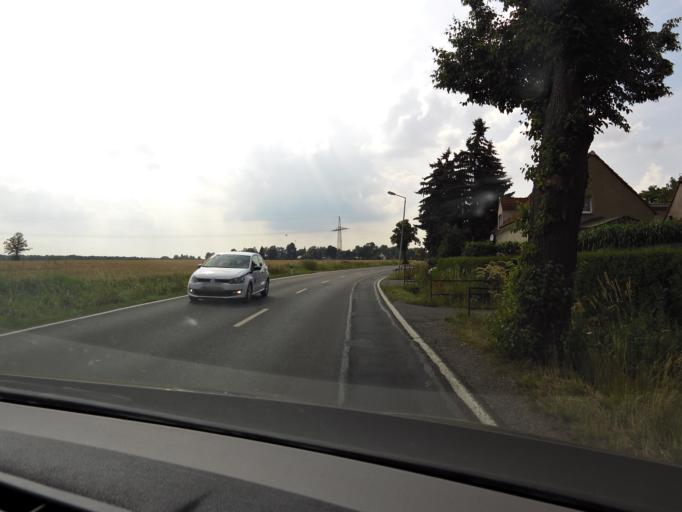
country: DE
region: Saxony
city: Belgershain
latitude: 51.2562
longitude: 12.5331
